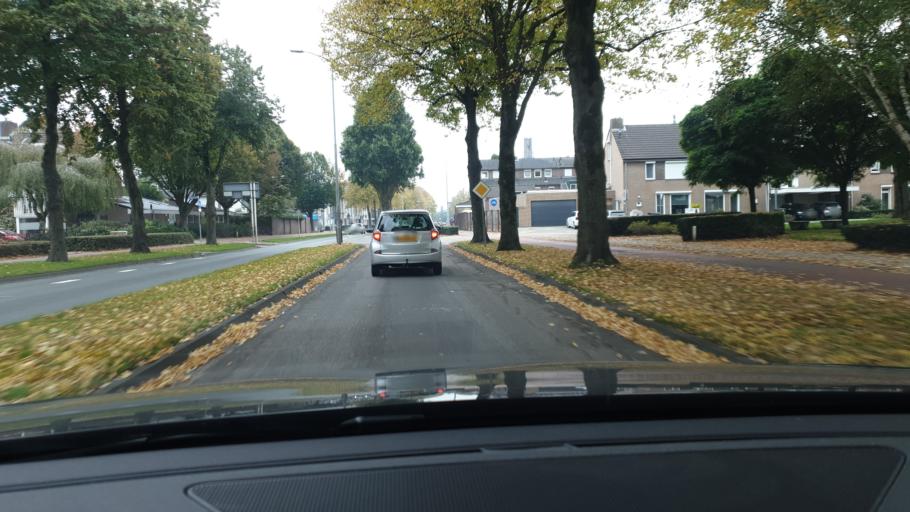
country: NL
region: North Brabant
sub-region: Gemeente Veldhoven
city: Veldhoven
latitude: 51.4171
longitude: 5.4069
